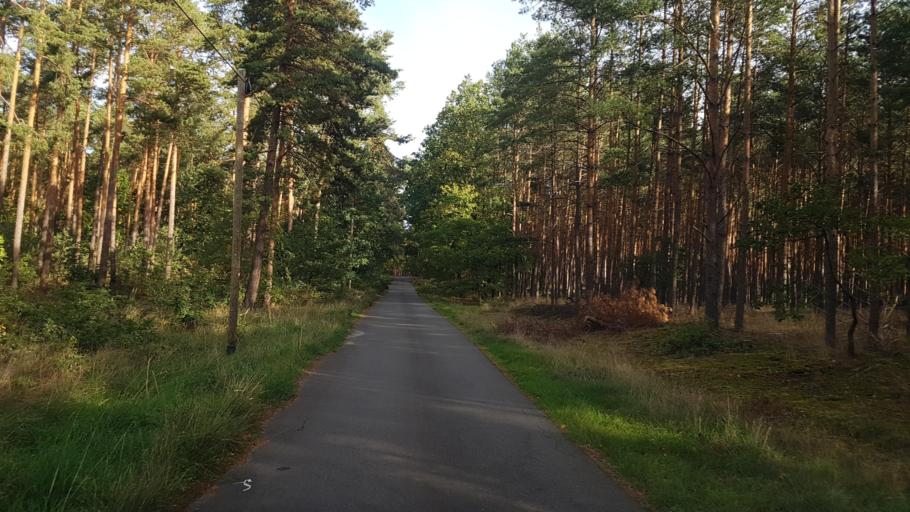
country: DE
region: Brandenburg
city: Drahnsdorf
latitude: 51.8416
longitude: 13.5345
